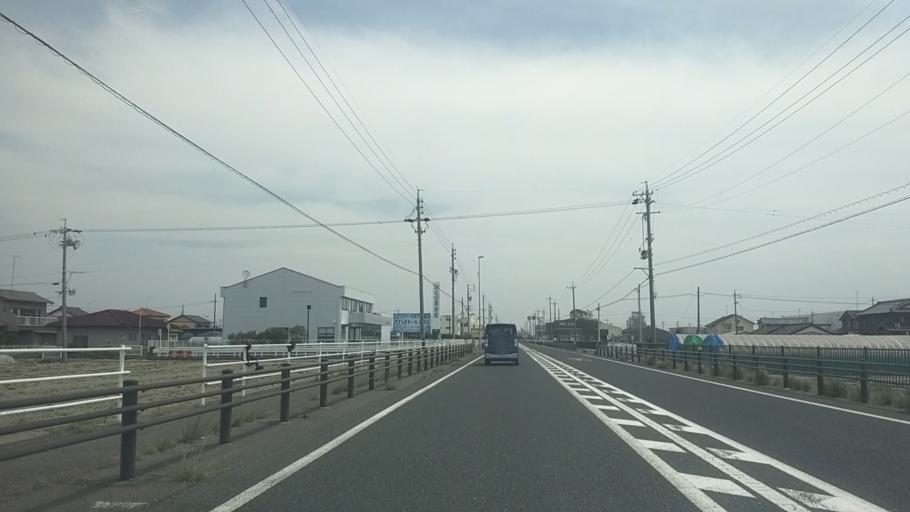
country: JP
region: Shizuoka
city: Hamamatsu
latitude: 34.6806
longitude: 137.6357
